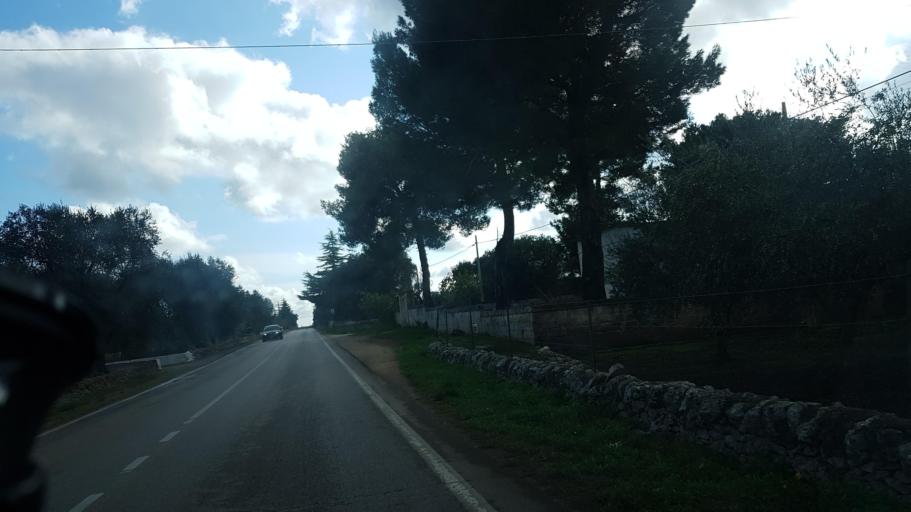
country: IT
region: Apulia
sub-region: Provincia di Brindisi
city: San Michele Salentino
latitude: 40.6664
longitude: 17.5987
